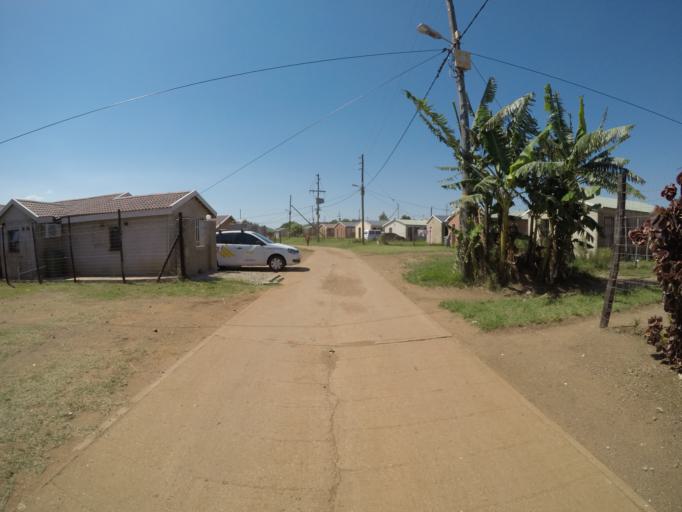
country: ZA
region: KwaZulu-Natal
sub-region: uThungulu District Municipality
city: Empangeni
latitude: -28.7670
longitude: 31.8793
